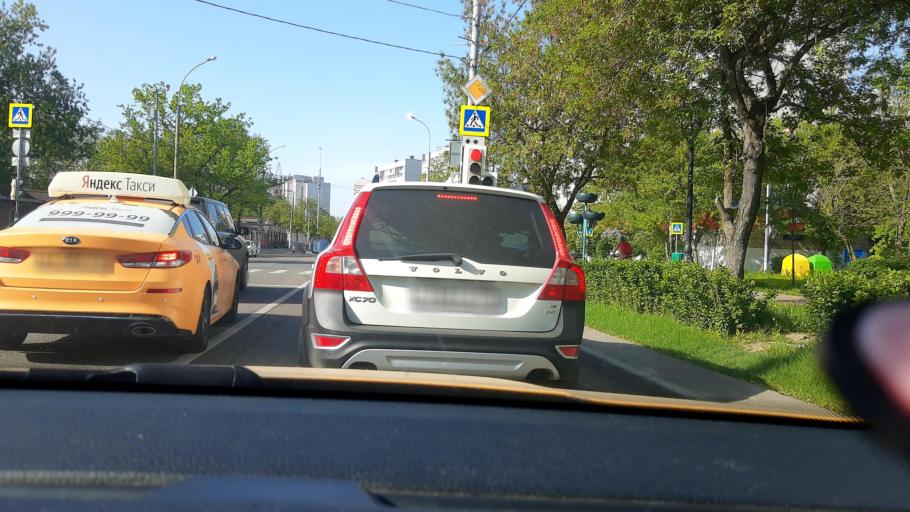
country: RU
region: Moscow
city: Pokrovskoye-Streshnevo
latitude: 55.8386
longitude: 37.4531
